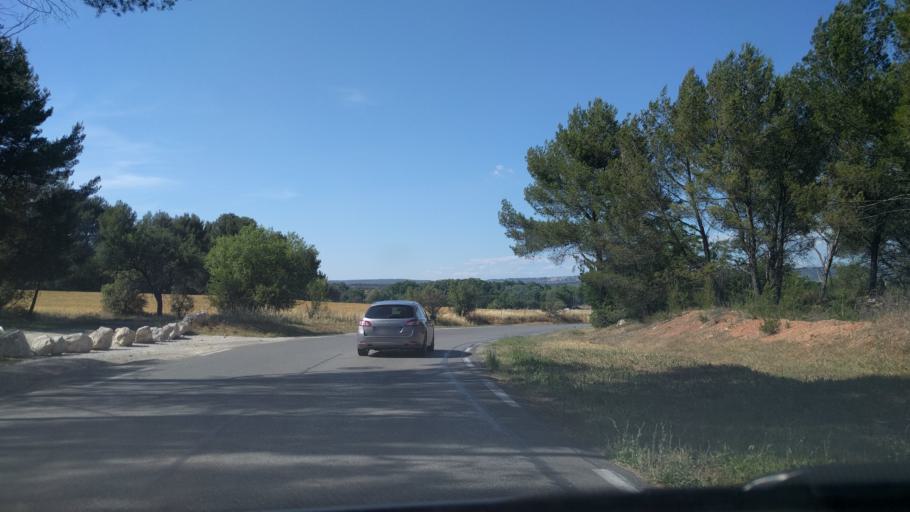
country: FR
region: Provence-Alpes-Cote d'Azur
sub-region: Departement des Bouches-du-Rhone
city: Cabries
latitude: 43.4977
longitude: 5.3494
